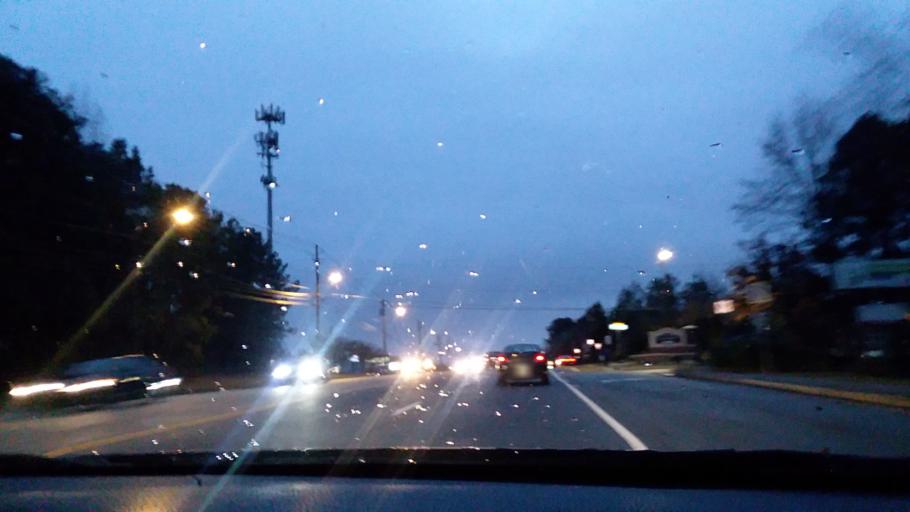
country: US
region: Georgia
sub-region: DeKalb County
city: Tucker
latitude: 33.8729
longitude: -84.1879
